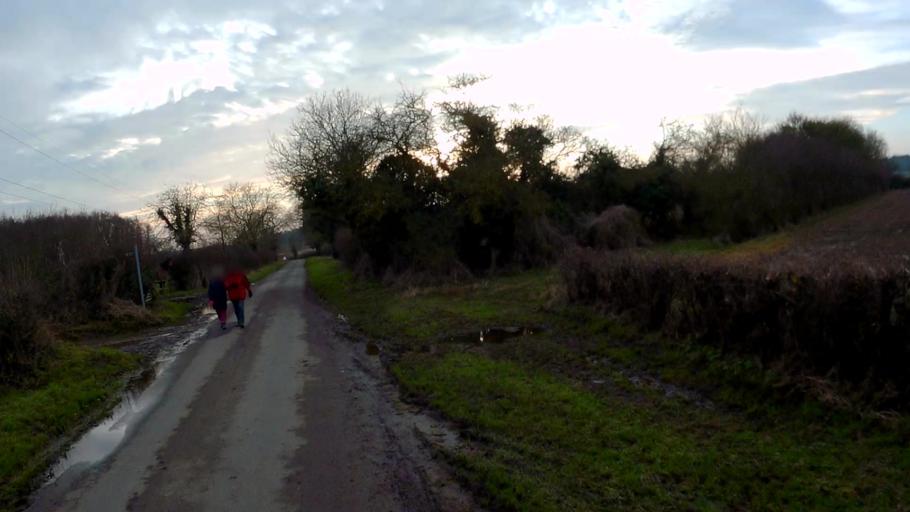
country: GB
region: England
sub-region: Lincolnshire
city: Bourne
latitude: 52.8240
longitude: -0.4058
